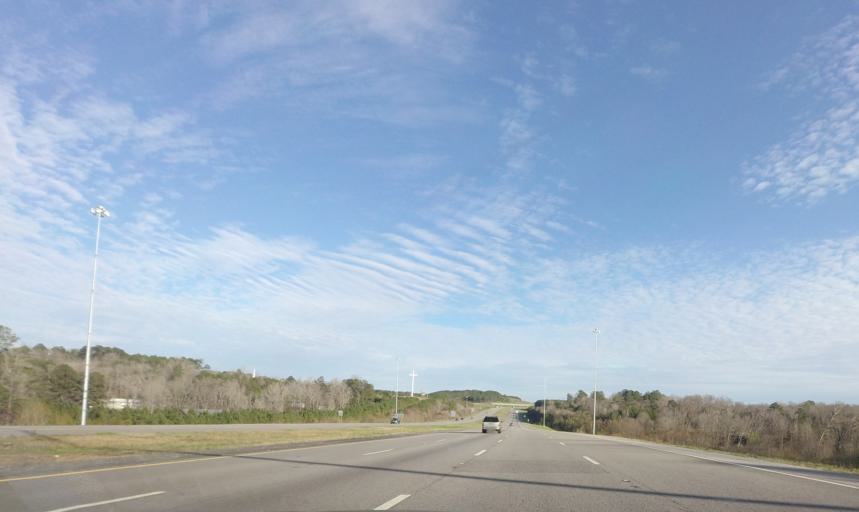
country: US
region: Alabama
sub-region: Walker County
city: Cordova
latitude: 33.7913
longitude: -87.2335
